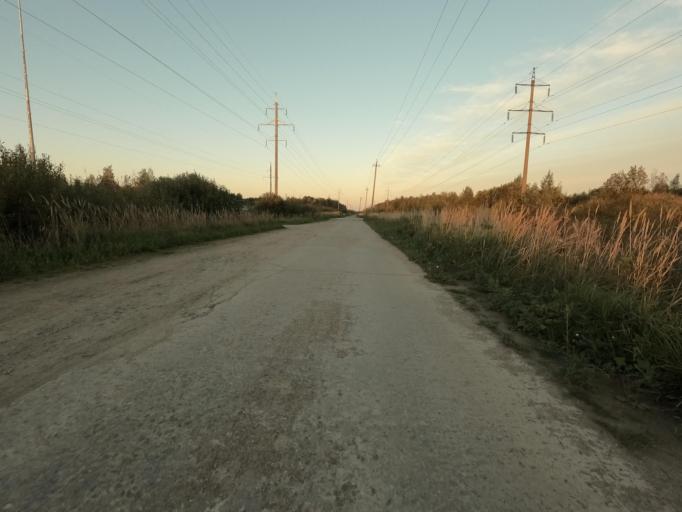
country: RU
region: Leningrad
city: Otradnoye
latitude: 59.7634
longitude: 30.8069
